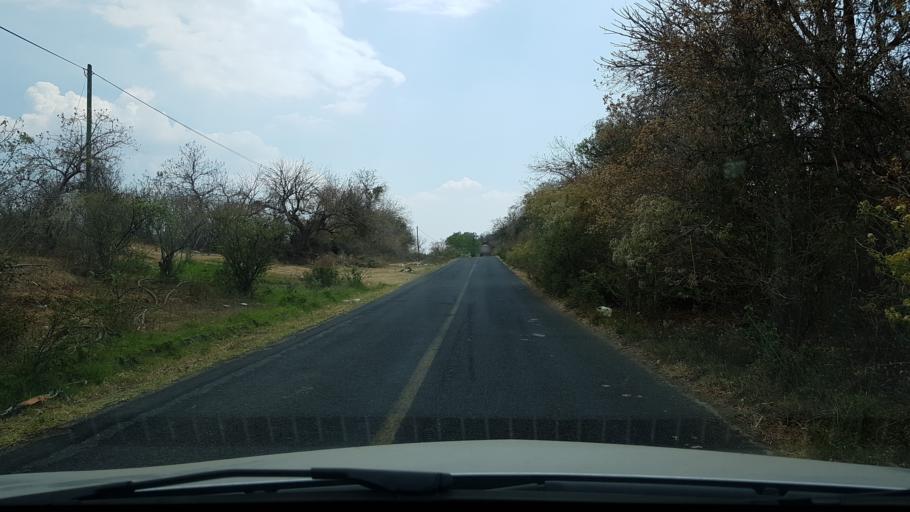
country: MX
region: Morelos
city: Tlacotepec
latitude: 18.8270
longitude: -98.7401
